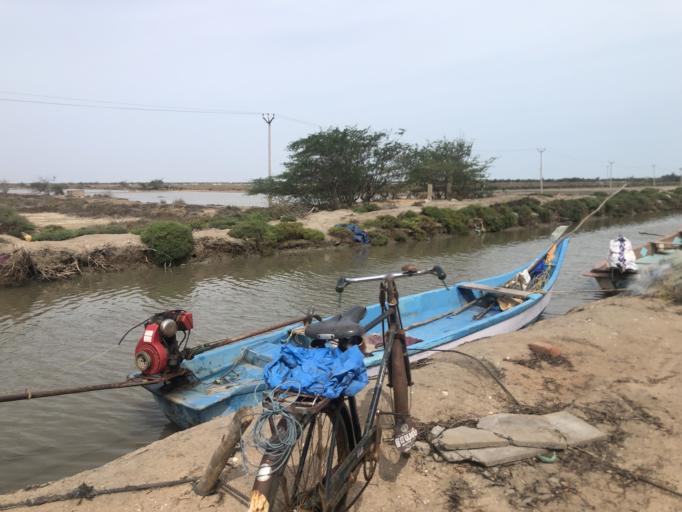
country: IN
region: Tamil Nadu
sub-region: Thanjavur
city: Adirampattinam
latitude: 10.3220
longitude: 79.3790
